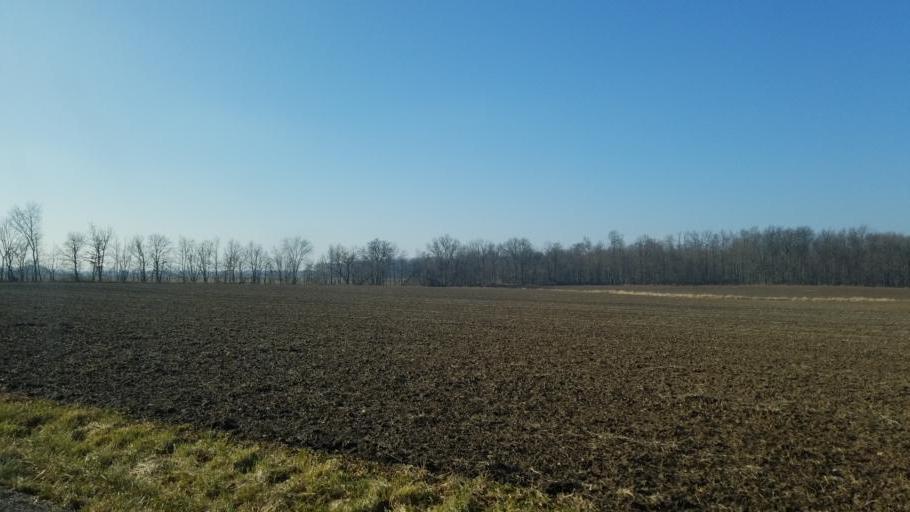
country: US
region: Ohio
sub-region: Seneca County
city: Tiffin
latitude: 41.0893
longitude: -83.1122
